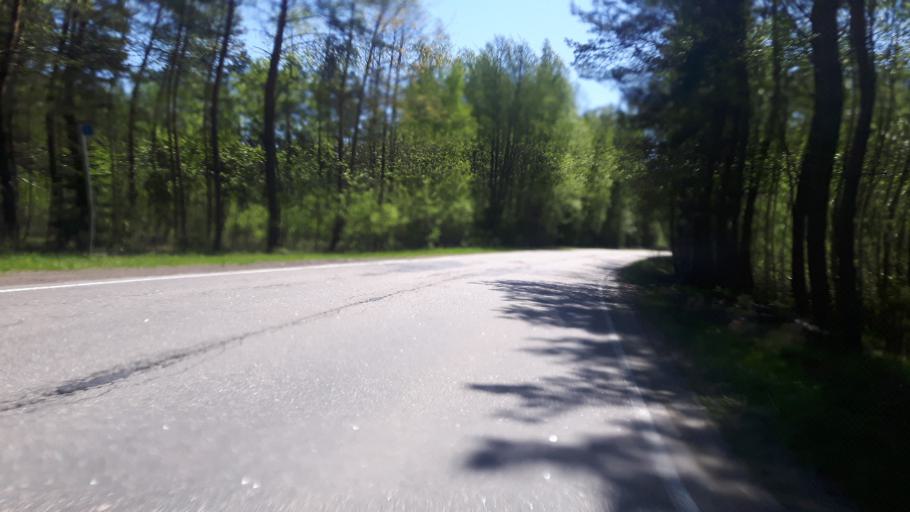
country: RU
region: Leningrad
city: Glebychevo
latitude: 60.3412
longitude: 28.8232
